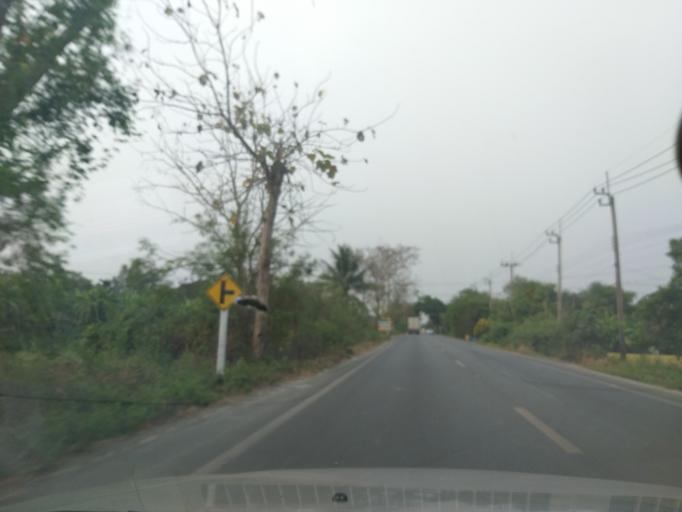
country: TH
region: Bangkok
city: Nong Chok
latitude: 13.9248
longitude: 100.8923
